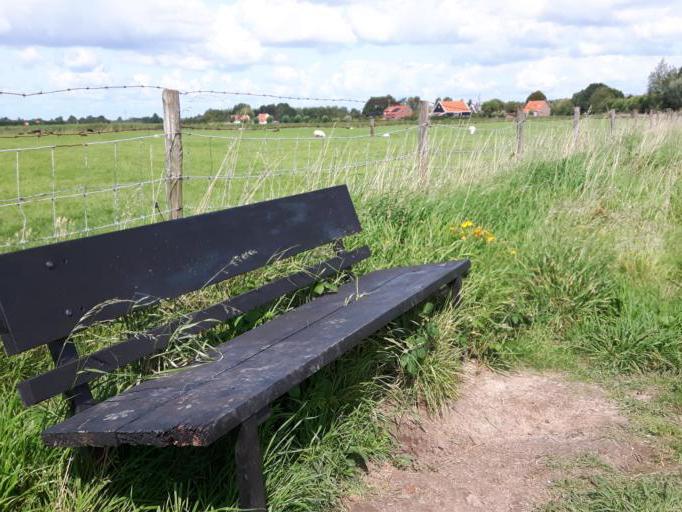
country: NL
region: Zeeland
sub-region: Gemeente Borsele
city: Borssele
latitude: 51.4681
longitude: 3.8025
